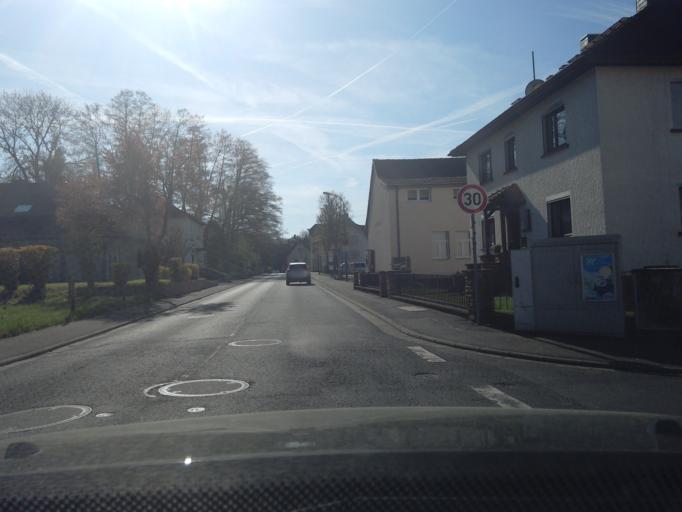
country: DE
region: Hesse
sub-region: Regierungsbezirk Darmstadt
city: Bad Soden-Salmunster
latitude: 50.3190
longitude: 9.3741
